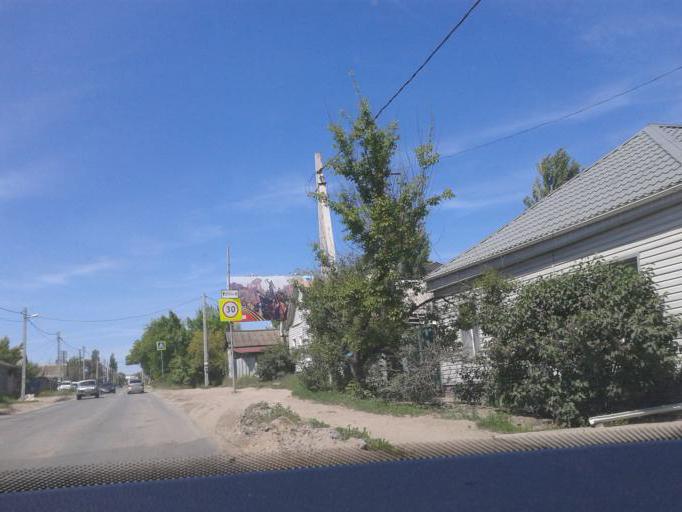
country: RU
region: Volgograd
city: Volgograd
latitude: 48.7513
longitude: 44.5417
